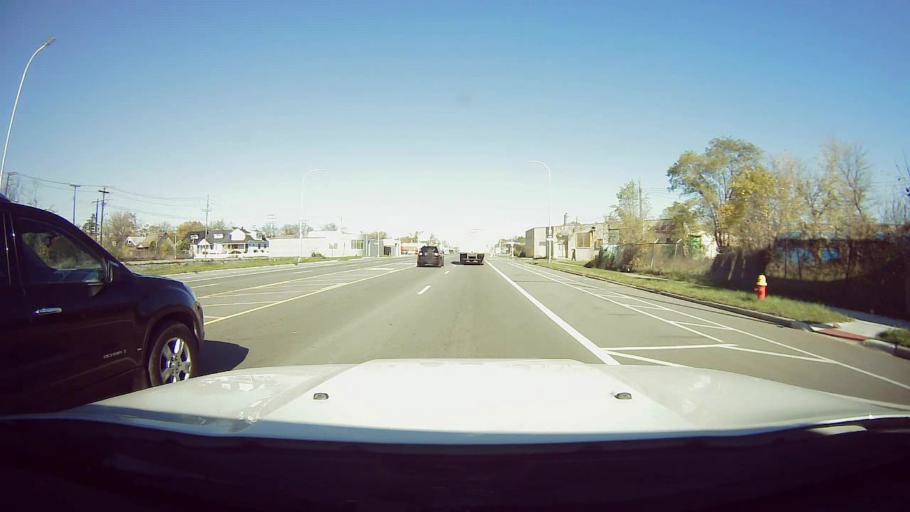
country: US
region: Michigan
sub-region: Wayne County
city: Dearborn
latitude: 42.3558
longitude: -83.1380
